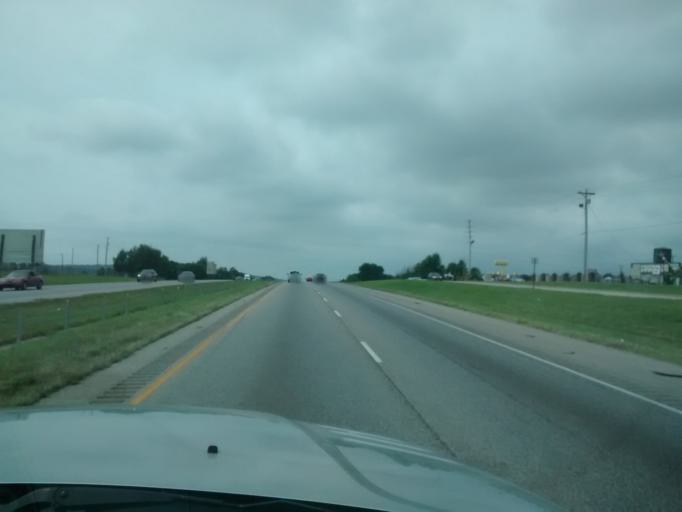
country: US
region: Arkansas
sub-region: Washington County
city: Johnson
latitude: 36.0985
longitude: -94.1862
